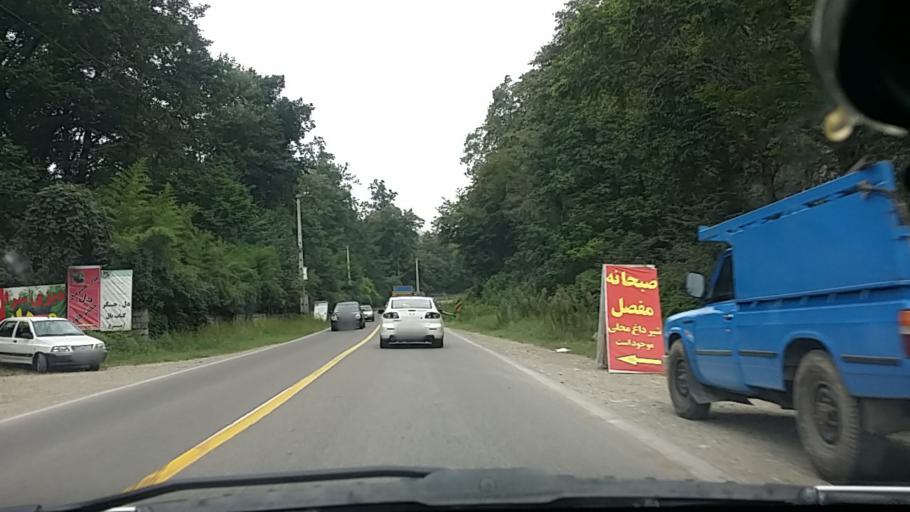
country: IR
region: Mazandaran
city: Chalus
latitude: 36.6070
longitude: 51.3865
